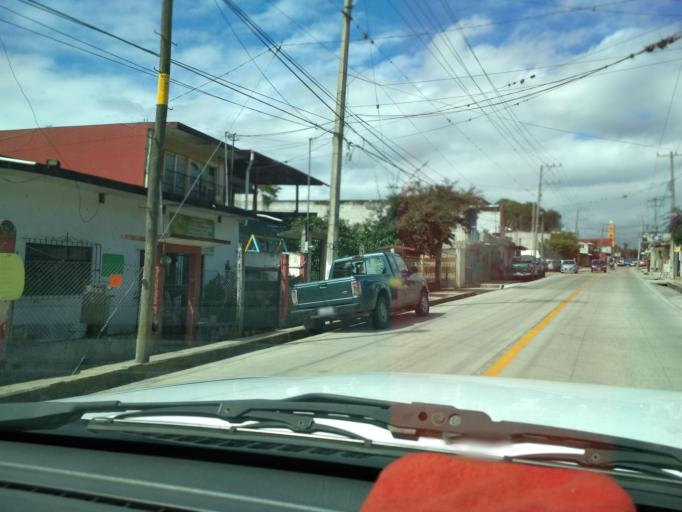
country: MX
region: Veracruz
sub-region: Coatepec
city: Las Lomas
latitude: 19.4362
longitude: -96.9201
